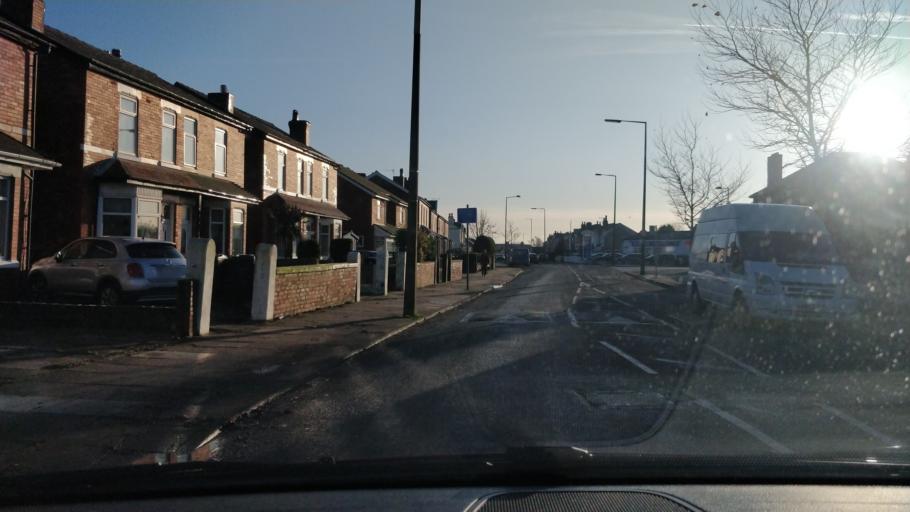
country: GB
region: England
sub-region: Lancashire
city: Banks
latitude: 53.6709
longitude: -2.9484
